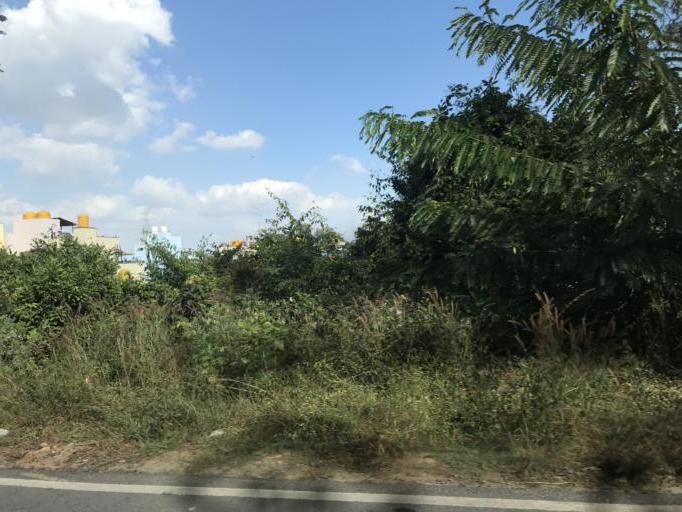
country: IN
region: Karnataka
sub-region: Bangalore Urban
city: Bangalore
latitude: 12.8175
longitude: 77.5769
